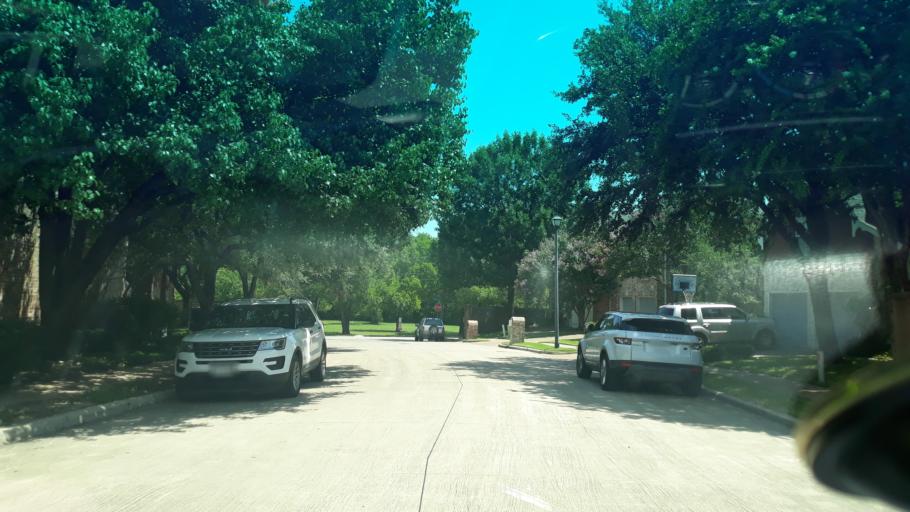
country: US
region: Texas
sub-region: Dallas County
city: Highland Park
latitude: 32.8158
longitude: -96.7315
